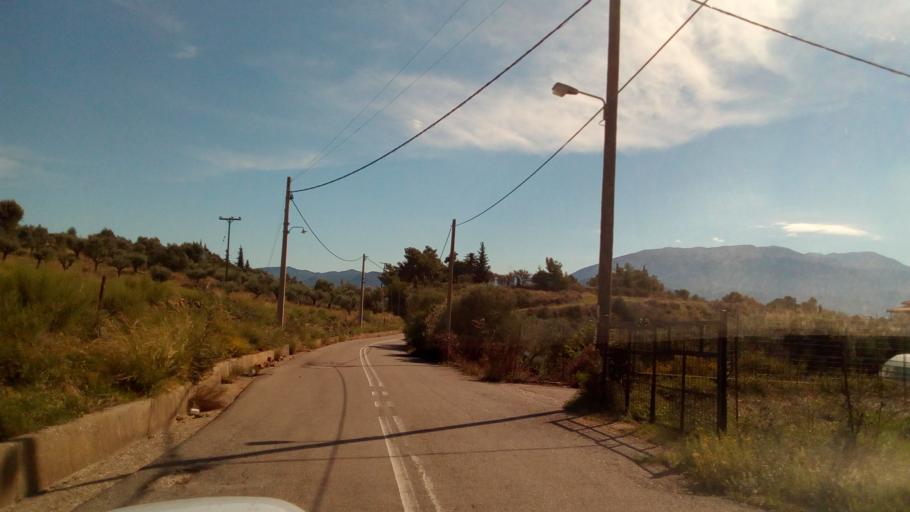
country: GR
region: West Greece
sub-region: Nomos Aitolias kai Akarnanias
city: Antirrio
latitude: 38.3688
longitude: 21.7761
